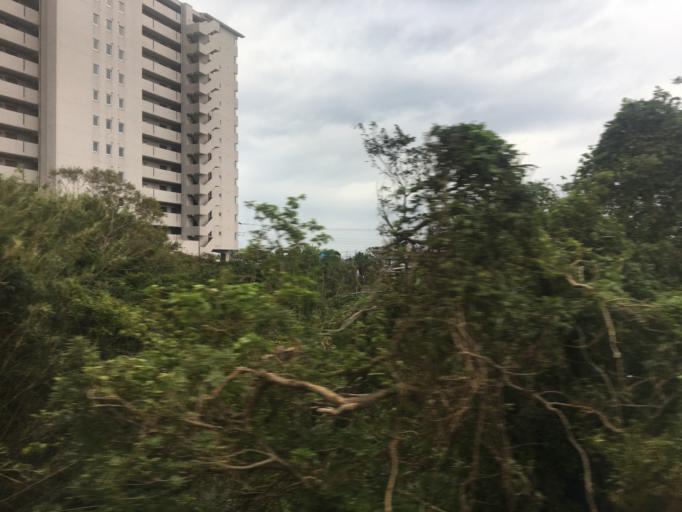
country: JP
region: Chiba
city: Tateyama
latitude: 35.0955
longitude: 139.8494
